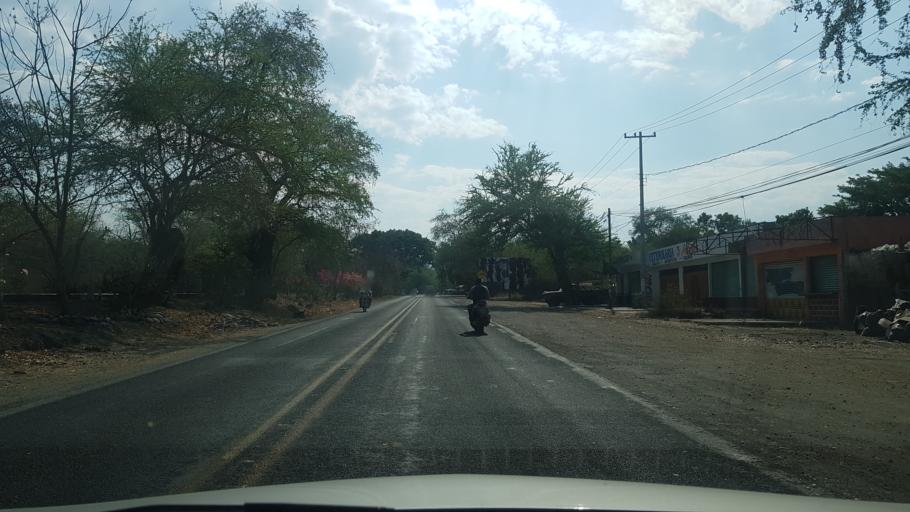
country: MX
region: Morelos
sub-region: Amacuzac
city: San Gabriel las Palmas
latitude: 18.6129
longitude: -99.3439
